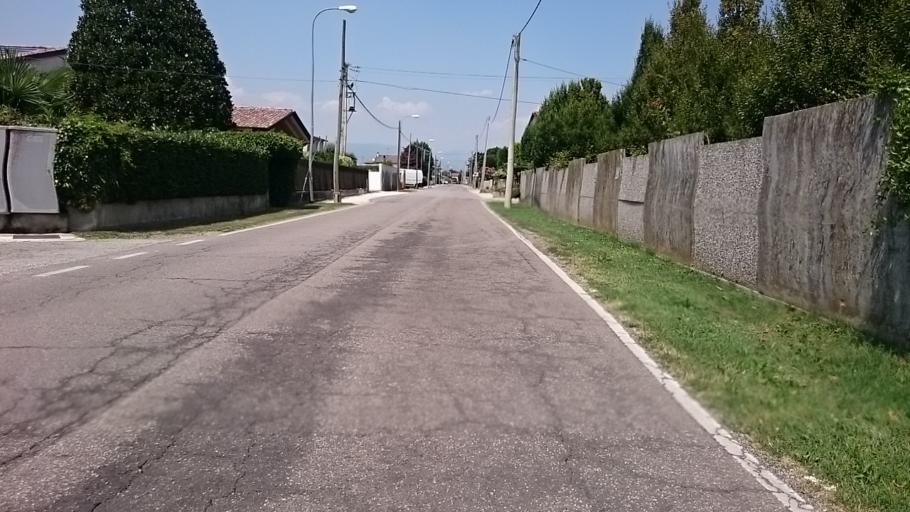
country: IT
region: Veneto
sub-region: Provincia di Padova
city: Fontaniva
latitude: 45.6572
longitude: 11.7576
